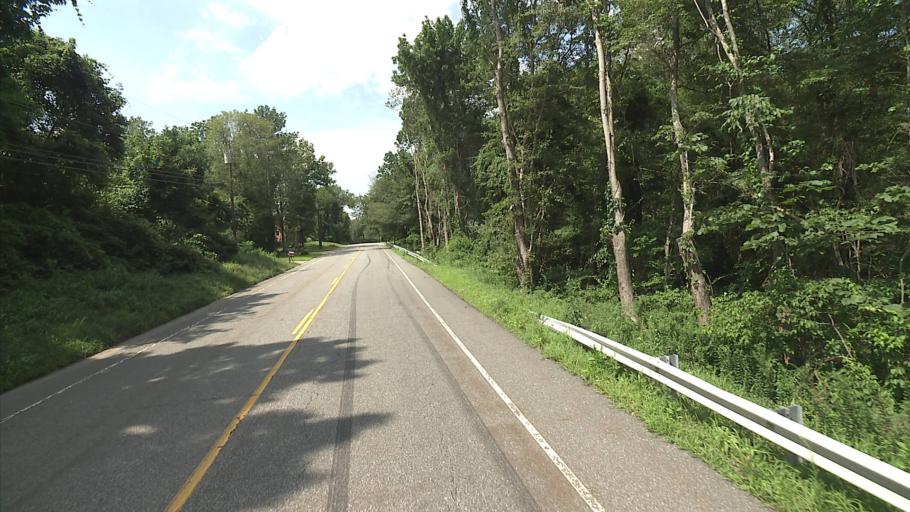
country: US
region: Connecticut
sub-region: New London County
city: Colchester
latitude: 41.5209
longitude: -72.2568
